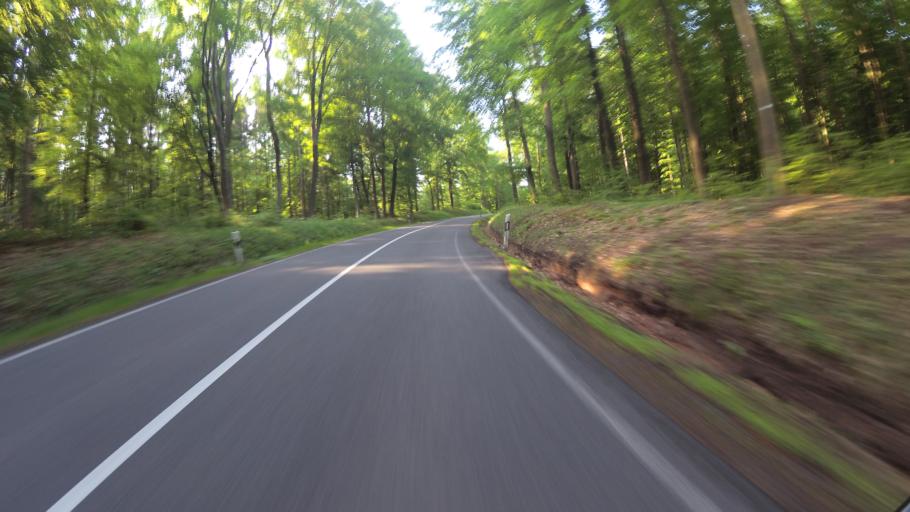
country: DE
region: Saarland
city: Neunkirchen
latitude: 49.3199
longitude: 7.1877
